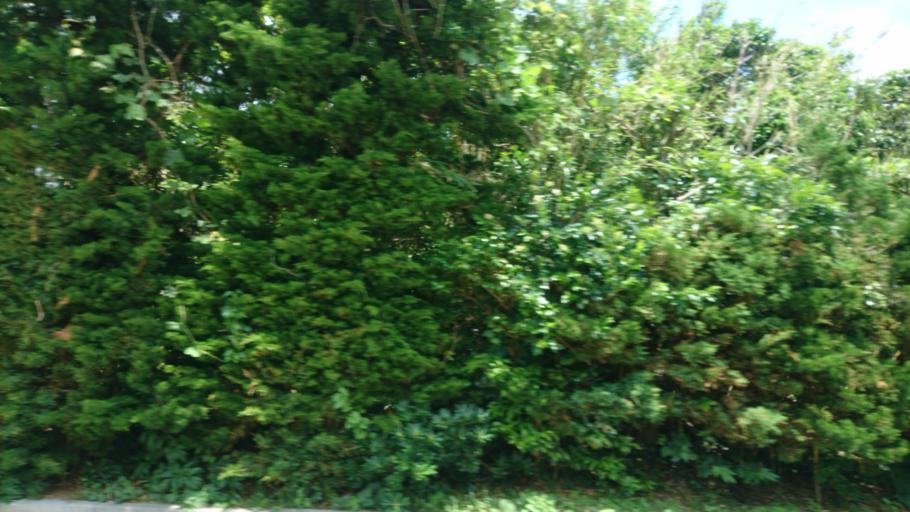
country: JP
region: Shizuoka
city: Shimoda
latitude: 34.4125
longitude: 139.2800
